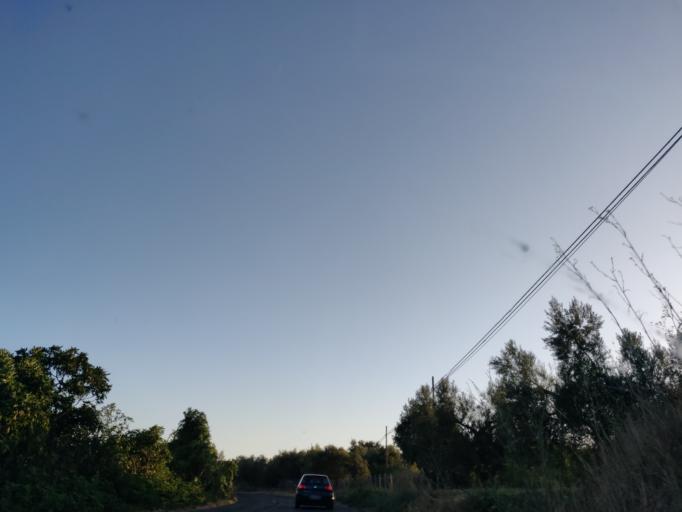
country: IT
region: Latium
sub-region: Provincia di Viterbo
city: Canino
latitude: 42.4527
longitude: 11.7377
